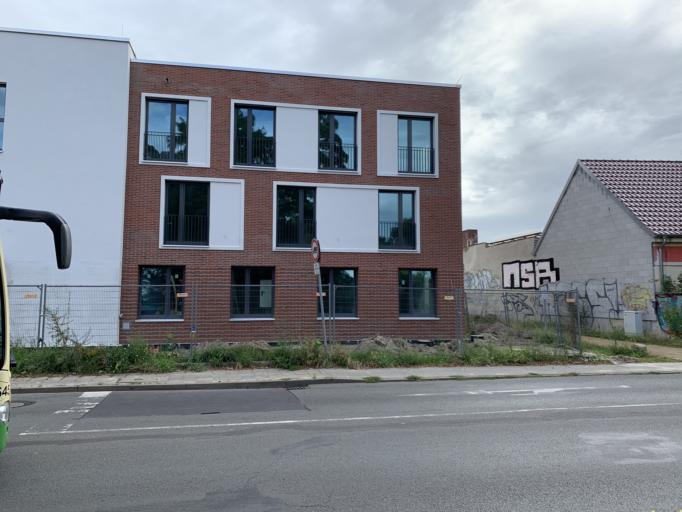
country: DE
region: Brandenburg
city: Brandenburg an der Havel
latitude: 52.4178
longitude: 12.5691
